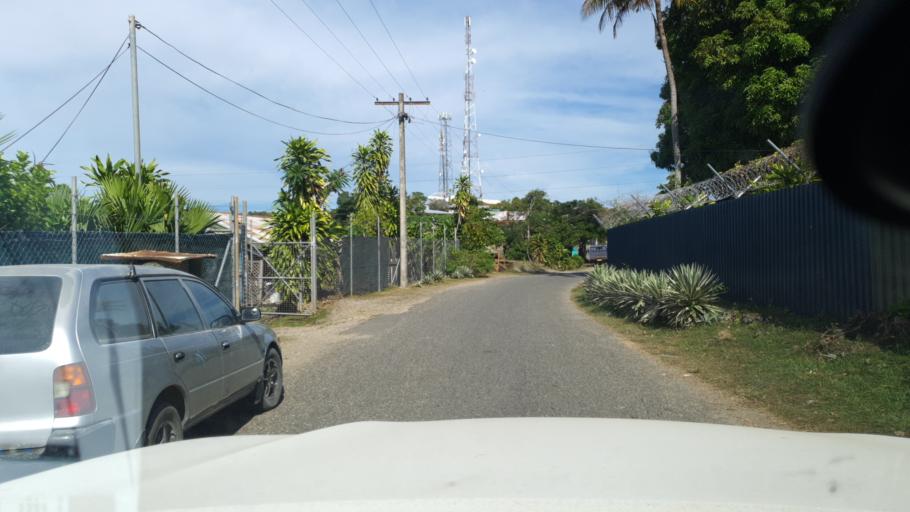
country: SB
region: Guadalcanal
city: Honiara
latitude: -9.4379
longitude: 159.9529
